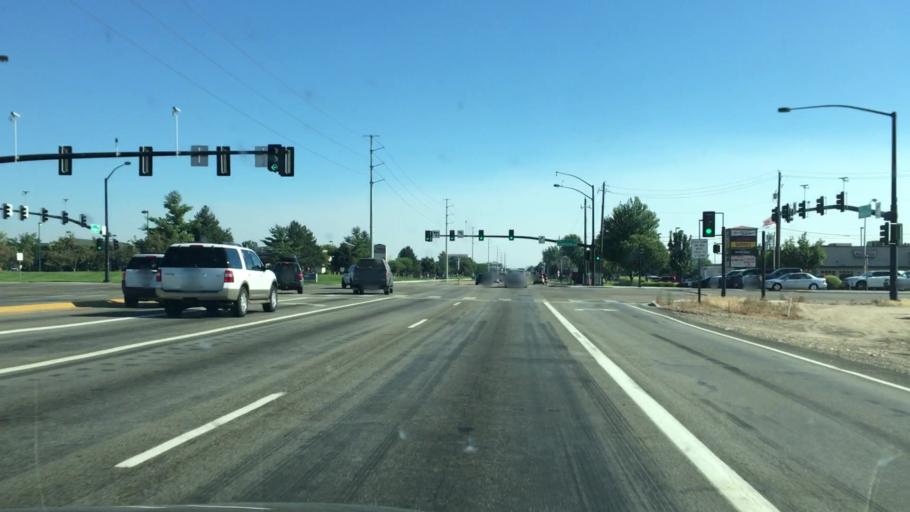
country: US
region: Idaho
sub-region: Ada County
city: Meridian
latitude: 43.6201
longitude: -116.3547
